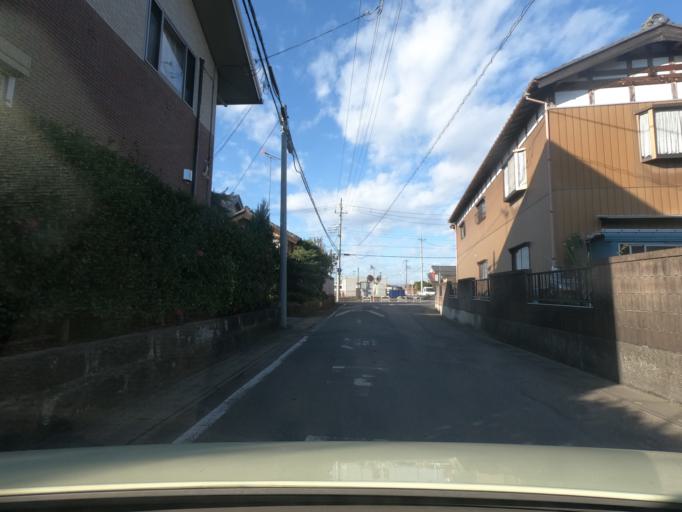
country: JP
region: Ibaraki
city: Koga
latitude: 36.2562
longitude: 139.7322
